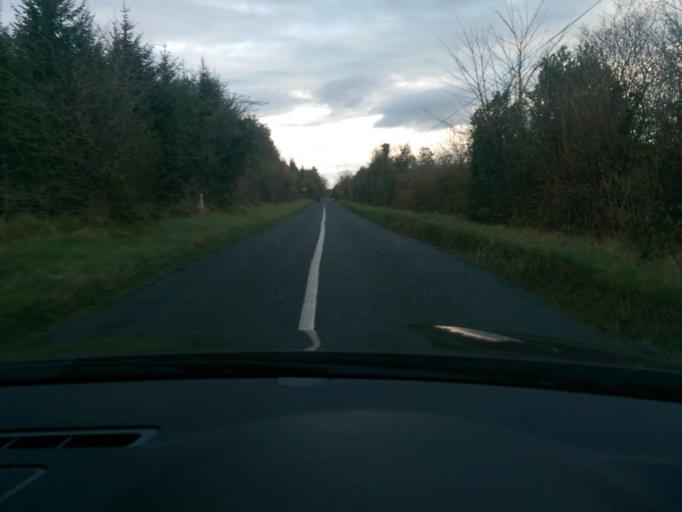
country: IE
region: Connaught
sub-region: County Galway
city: Athenry
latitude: 53.4511
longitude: -8.5526
